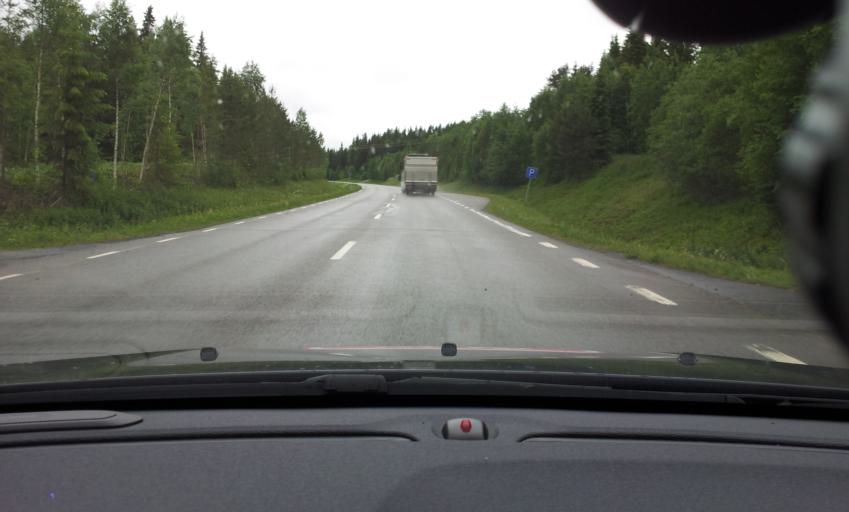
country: SE
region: Jaemtland
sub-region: OEstersunds Kommun
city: Lit
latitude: 63.6545
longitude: 14.6490
